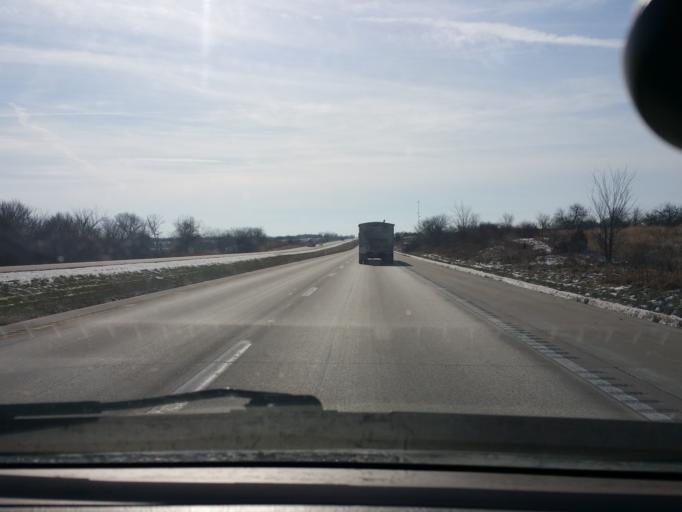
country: US
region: Missouri
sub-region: Clinton County
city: Cameron
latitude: 39.6272
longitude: -94.2460
